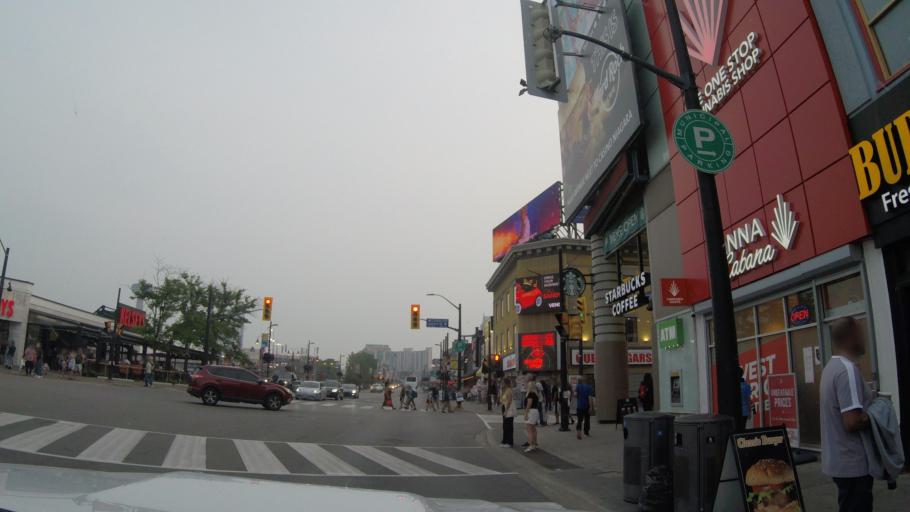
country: CA
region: Ontario
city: Niagara Falls
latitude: 43.0921
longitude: -79.0757
